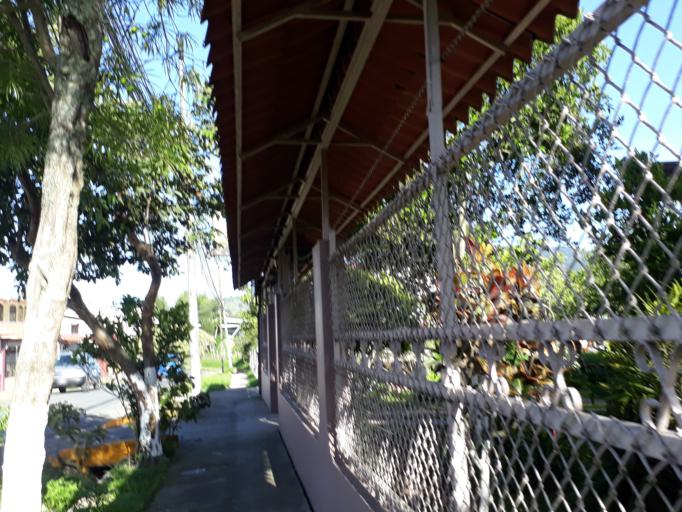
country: CR
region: Cartago
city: Cartago
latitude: 9.8735
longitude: -83.9420
